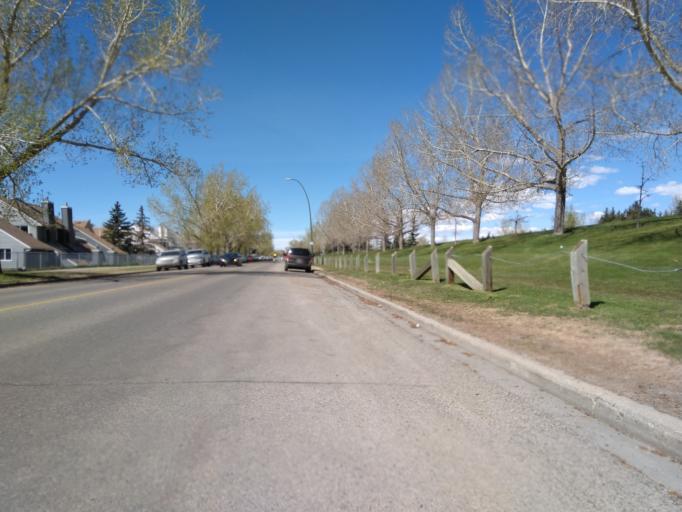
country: CA
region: Alberta
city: Calgary
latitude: 51.0128
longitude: -114.1597
